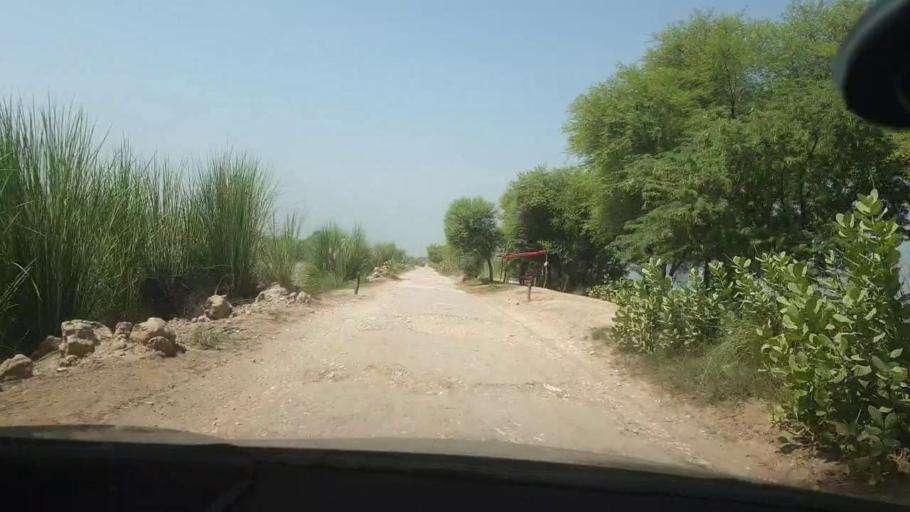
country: PK
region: Sindh
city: Shahdadkot
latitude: 27.7228
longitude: 67.9531
